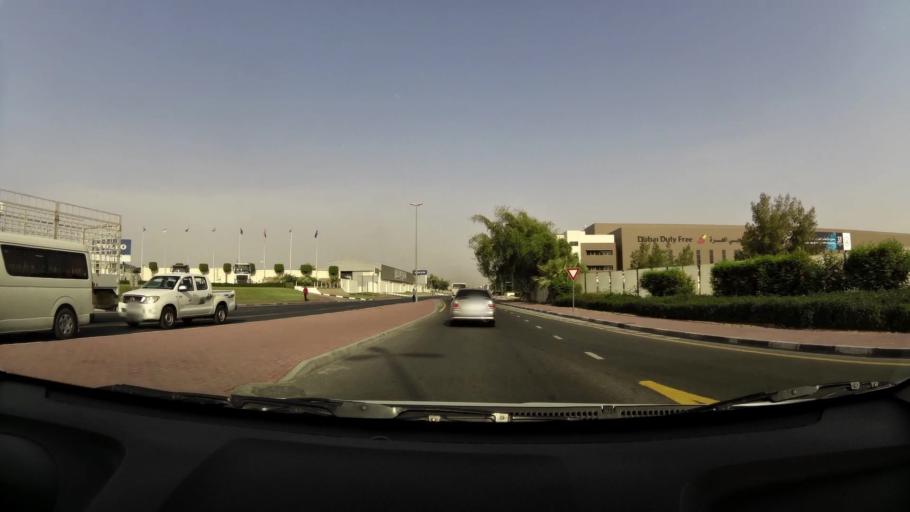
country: AE
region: Ash Shariqah
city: Sharjah
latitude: 25.2335
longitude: 55.3587
